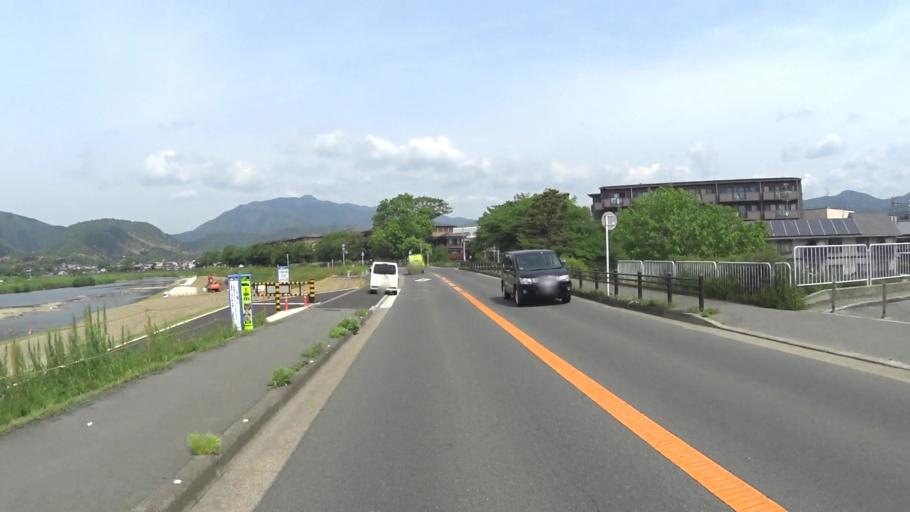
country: JP
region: Kyoto
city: Muko
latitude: 35.0103
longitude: 135.6893
